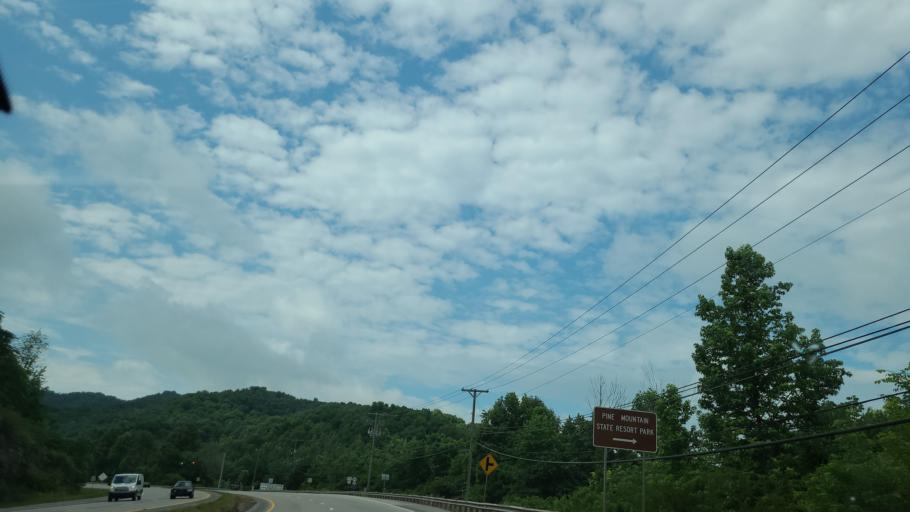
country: US
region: Kentucky
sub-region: Bell County
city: Pineville
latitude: 36.7390
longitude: -83.6959
